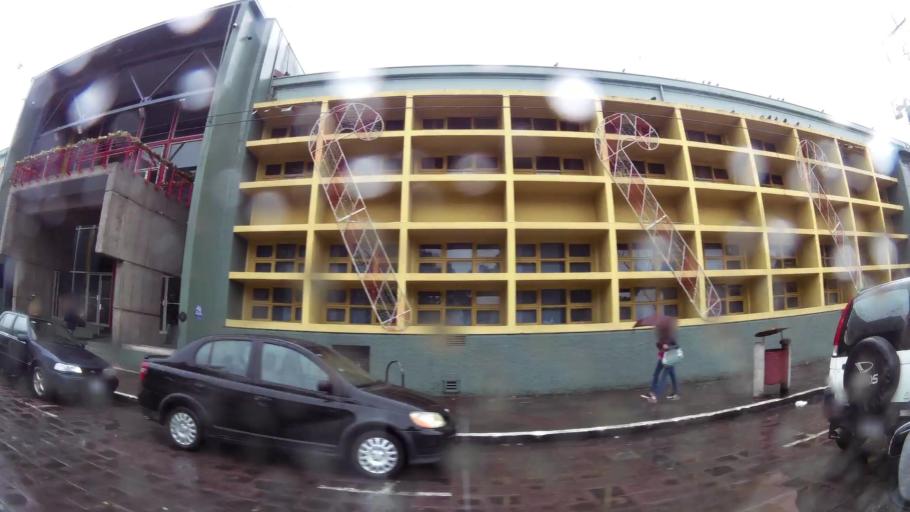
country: CR
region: Cartago
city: Cartago
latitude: 9.8647
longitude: -83.9207
